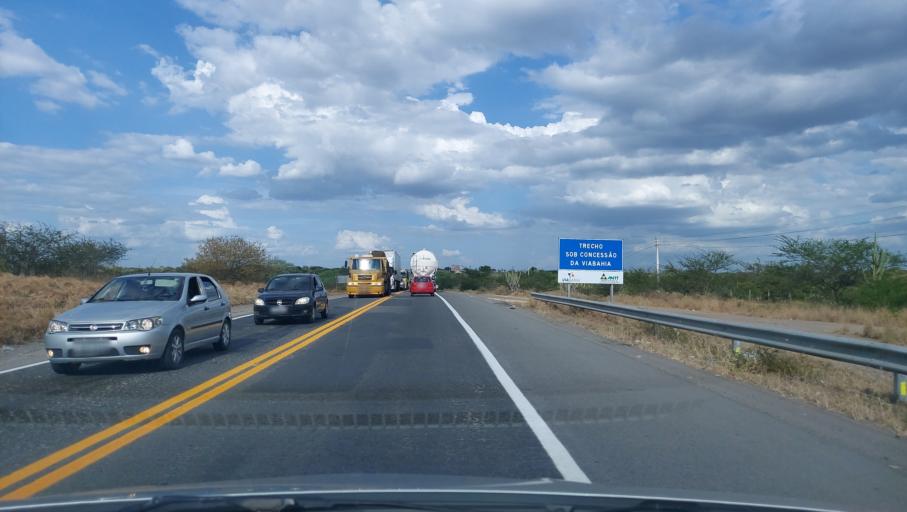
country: BR
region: Bahia
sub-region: Castro Alves
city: Castro Alves
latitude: -12.5793
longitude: -39.5116
